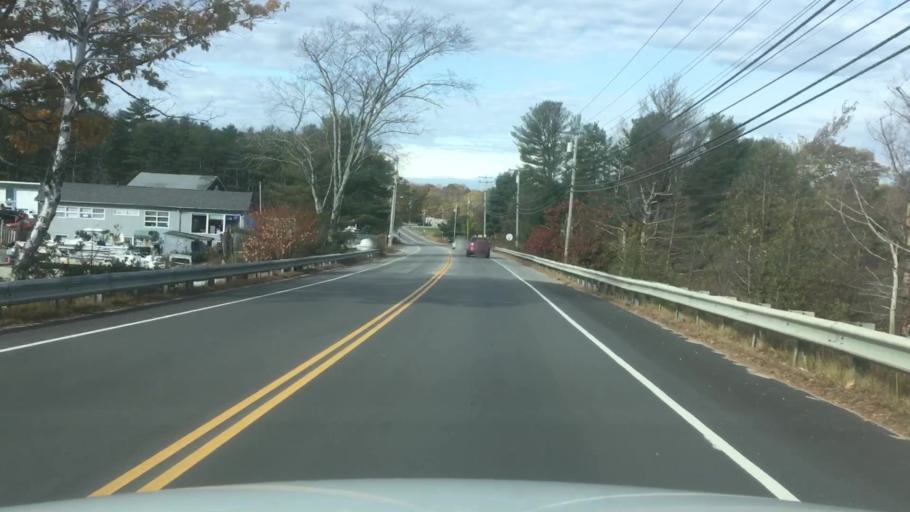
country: US
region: Maine
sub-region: Sagadahoc County
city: Bath
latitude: 43.9110
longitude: -69.8688
